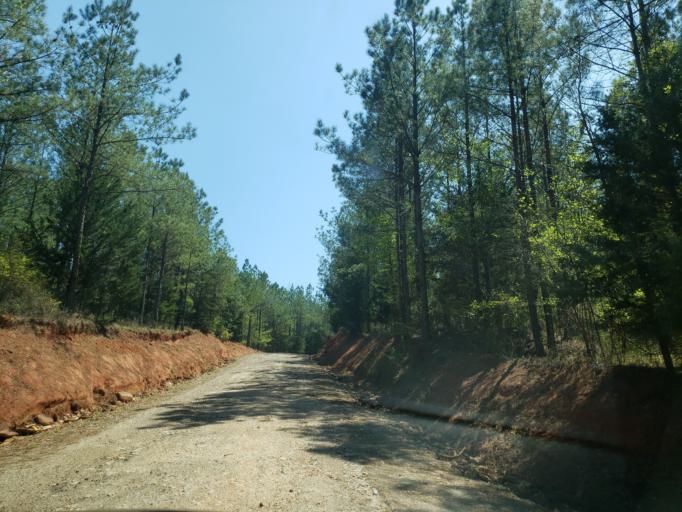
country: US
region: Alabama
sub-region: Tallapoosa County
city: Camp Hill
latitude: 32.6519
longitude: -85.6556
